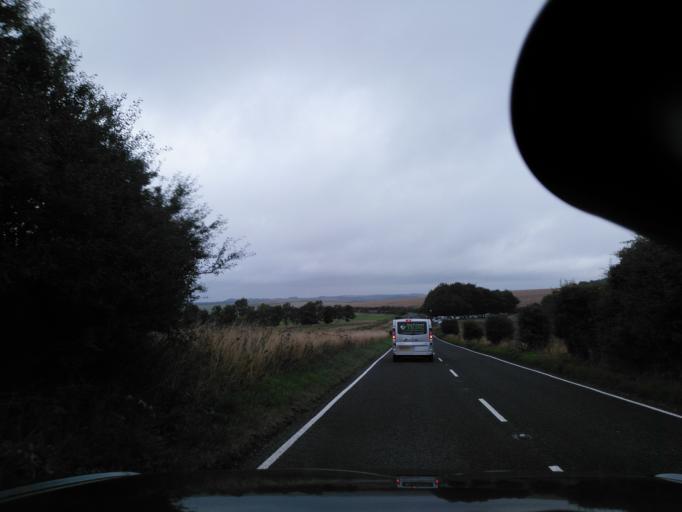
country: GB
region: England
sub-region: Wiltshire
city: Chicklade
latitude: 51.1407
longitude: -2.1618
